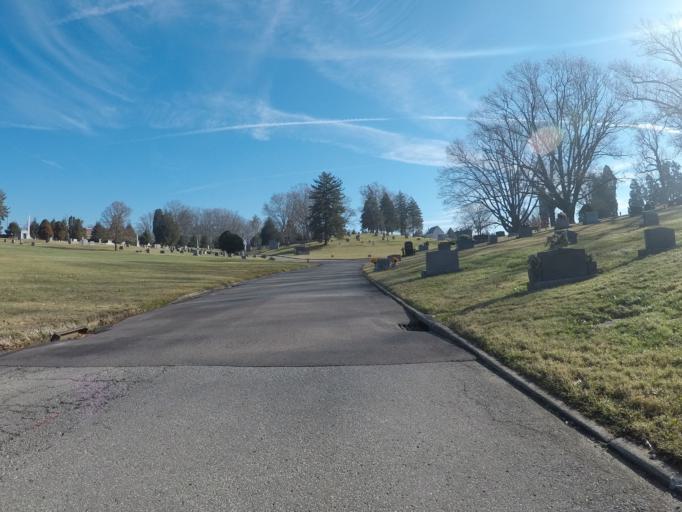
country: US
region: West Virginia
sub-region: Cabell County
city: Huntington
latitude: 38.4104
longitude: -82.4157
